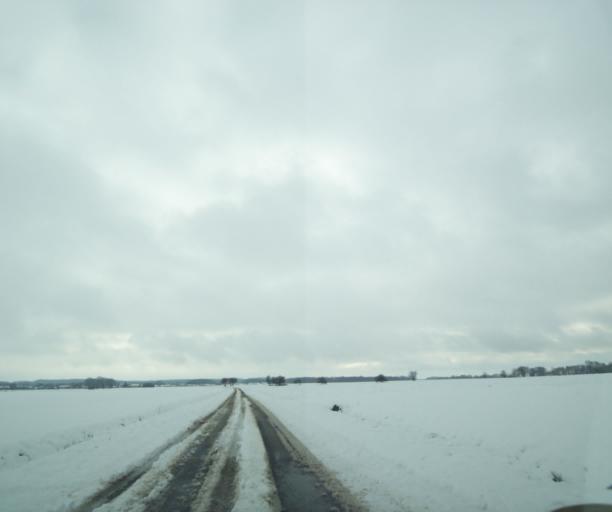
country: FR
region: Champagne-Ardenne
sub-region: Departement de la Haute-Marne
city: Montier-en-Der
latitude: 48.5004
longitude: 4.6861
